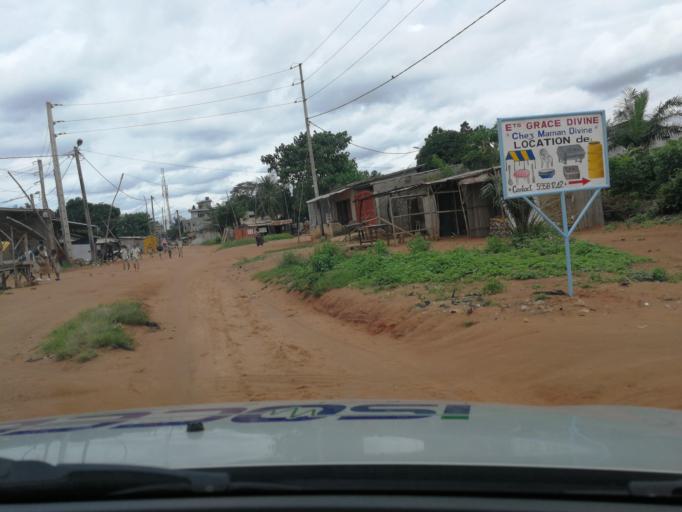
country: BJ
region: Atlantique
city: Abomey-Calavi
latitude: 6.4358
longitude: 2.3060
